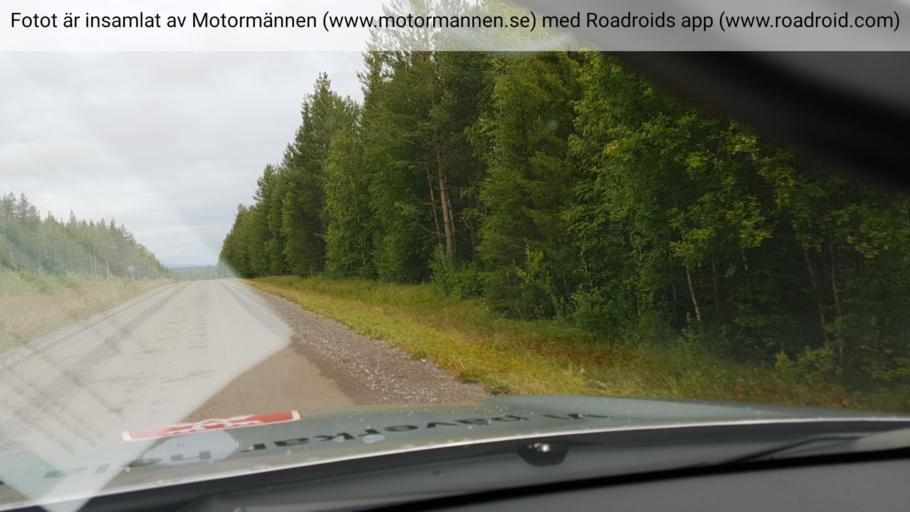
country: SE
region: Norrbotten
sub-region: Alvsbyns Kommun
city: AElvsbyn
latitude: 66.0174
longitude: 21.0376
